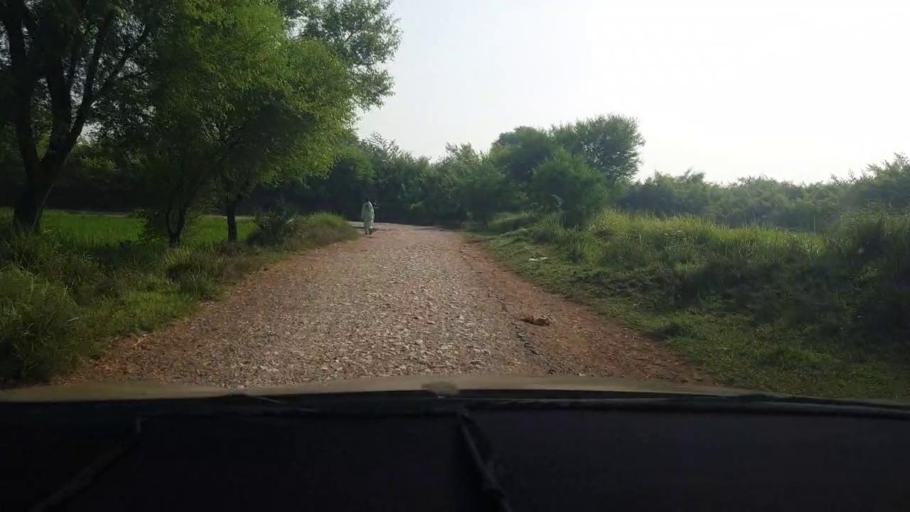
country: PK
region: Sindh
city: Kambar
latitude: 27.5987
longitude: 68.1108
